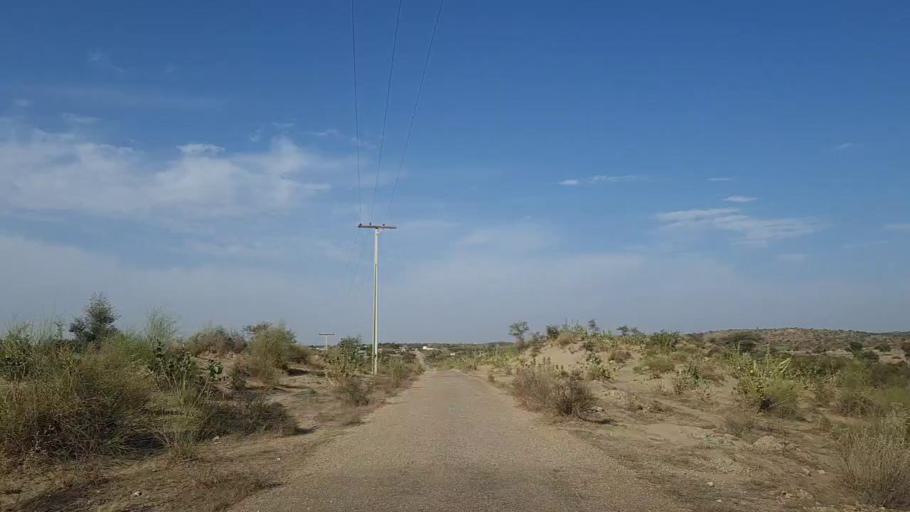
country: PK
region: Sindh
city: Naukot
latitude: 24.8588
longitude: 69.5253
